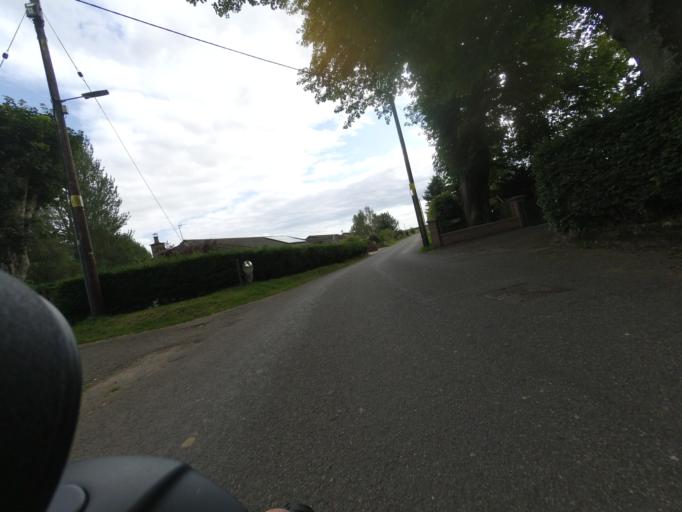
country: GB
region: Scotland
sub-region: Aberdeenshire
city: Laurencekirk
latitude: 56.8472
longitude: -2.5685
